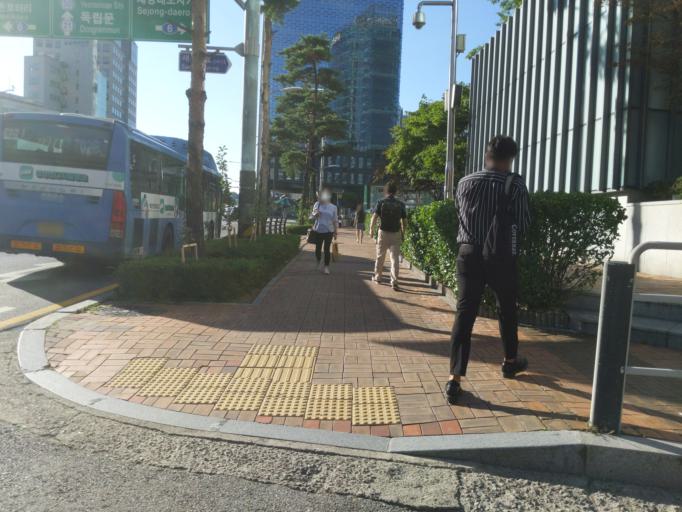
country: KR
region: Seoul
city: Seoul
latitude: 37.5651
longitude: 126.9676
